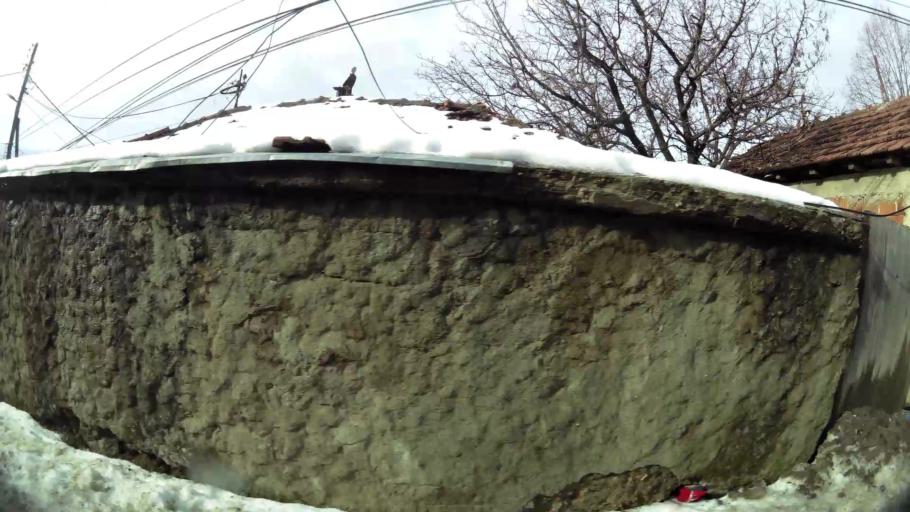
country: XK
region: Pristina
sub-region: Komuna e Prishtines
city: Pristina
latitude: 42.6722
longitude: 21.1752
